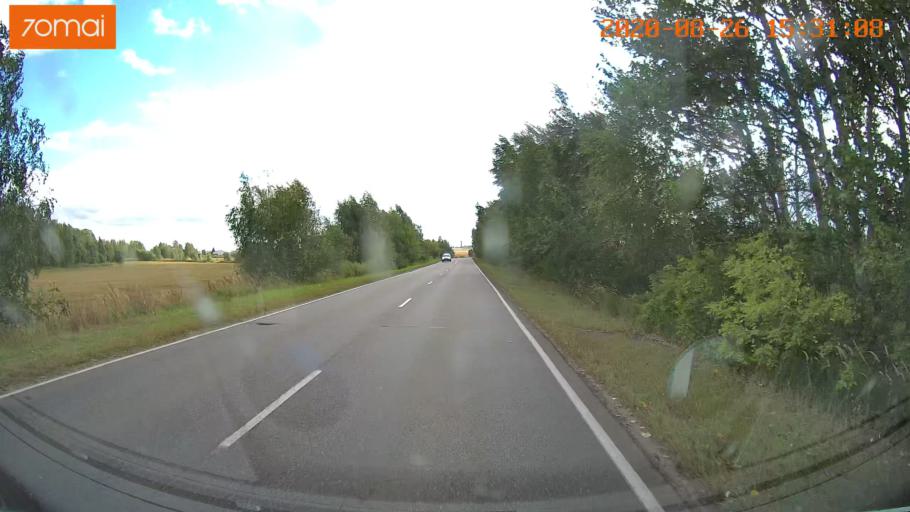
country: RU
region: Tula
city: Severo-Zadonsk
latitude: 54.0832
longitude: 38.3903
